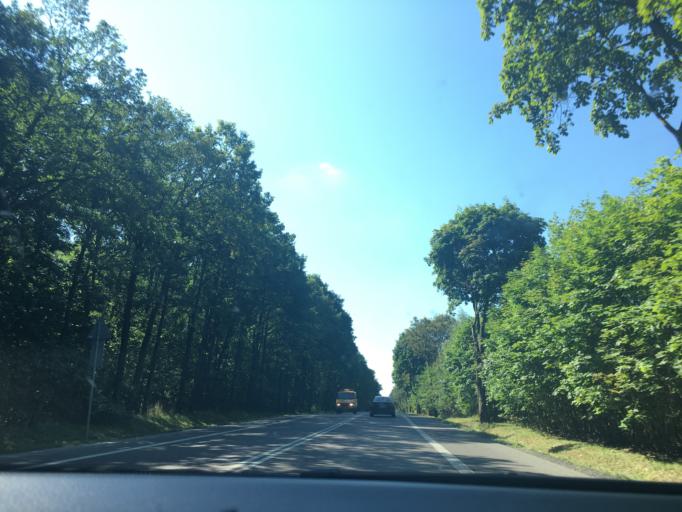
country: PL
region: Lublin Voivodeship
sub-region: Powiat lubelski
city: Niemce
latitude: 51.3962
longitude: 22.6366
